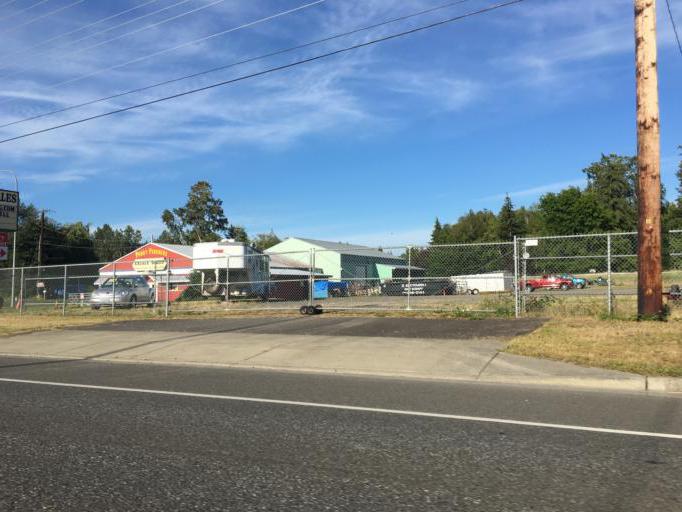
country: US
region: Washington
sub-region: Whatcom County
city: Bellingham
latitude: 48.8181
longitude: -122.4859
